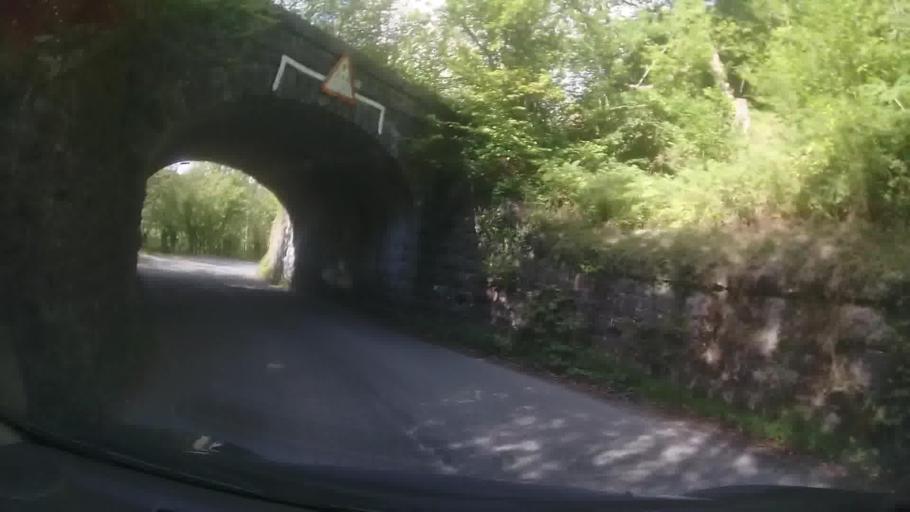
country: GB
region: Wales
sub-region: Merthyr Tydfil County Borough
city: Merthyr Tydfil
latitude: 51.7864
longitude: -3.3628
